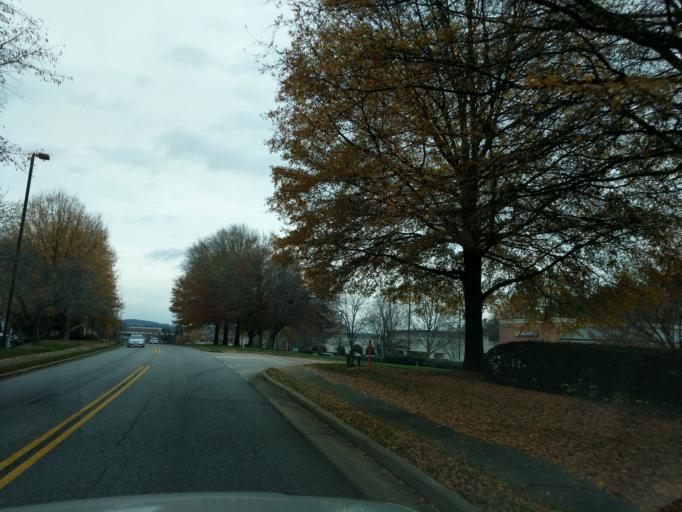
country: US
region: Georgia
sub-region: Fulton County
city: Alpharetta
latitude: 34.0343
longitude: -84.2903
